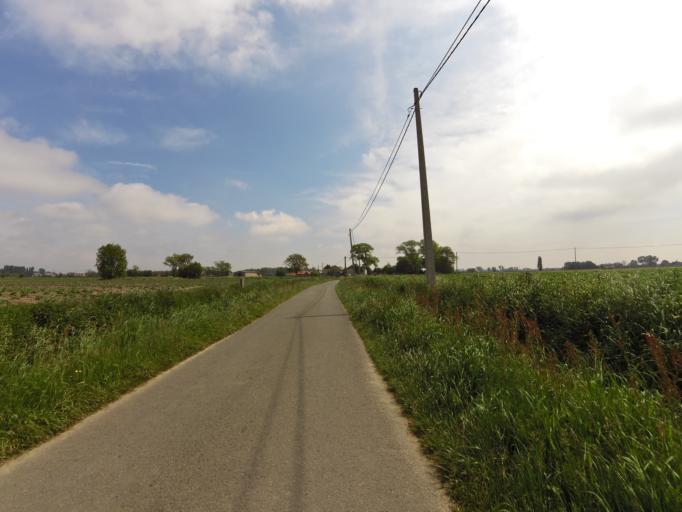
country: BE
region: Flanders
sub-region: Provincie West-Vlaanderen
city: Koekelare
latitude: 51.1182
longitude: 2.9873
